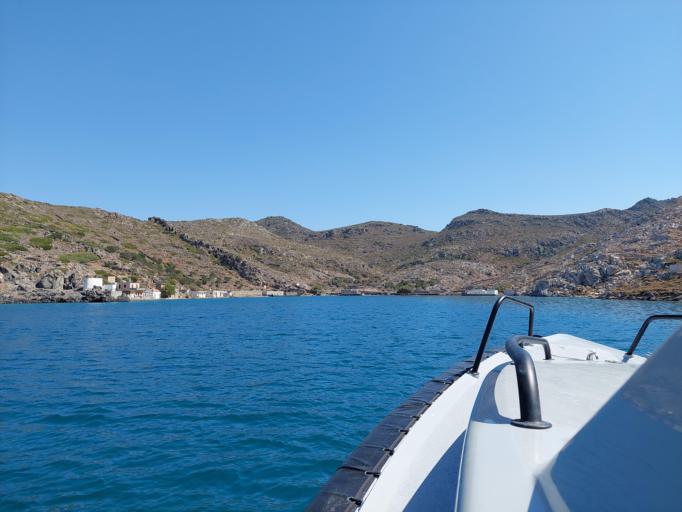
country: GR
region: South Aegean
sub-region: Nomos Dodekanisou
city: Karpathos
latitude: 35.8212
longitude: 27.2186
